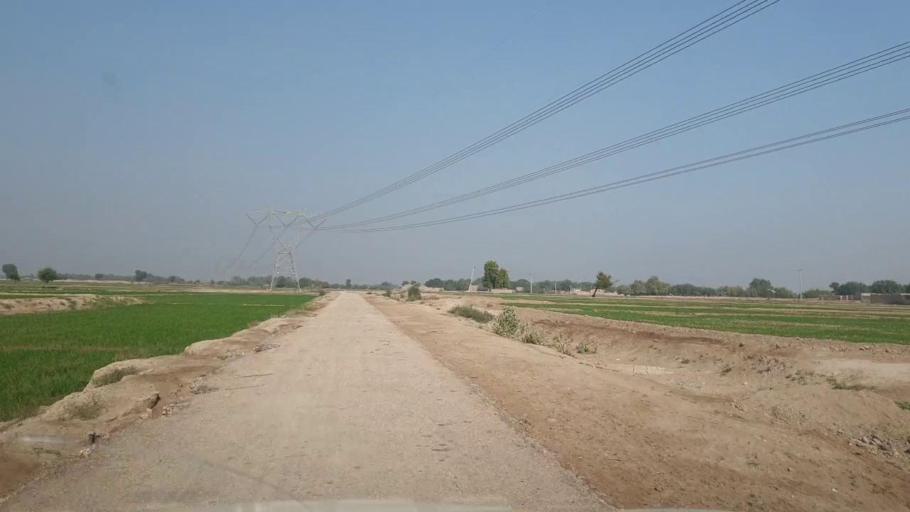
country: PK
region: Sindh
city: Bhan
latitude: 26.5439
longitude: 67.7483
